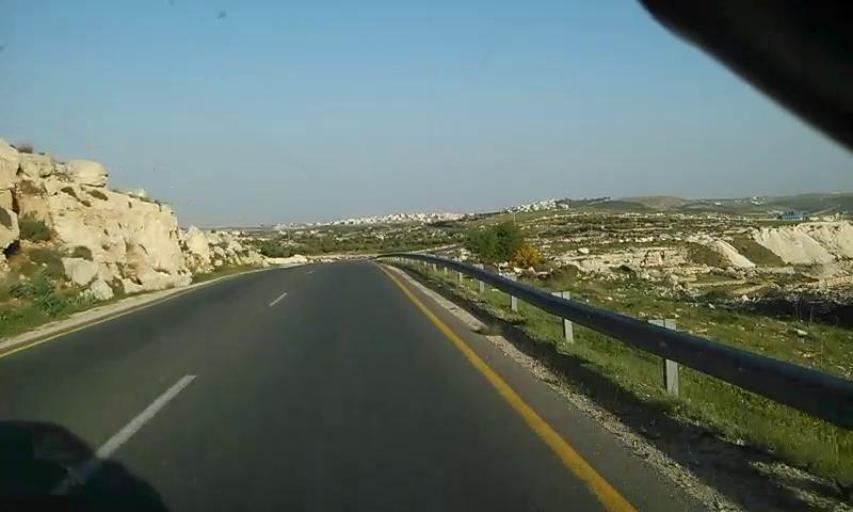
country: PS
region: West Bank
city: Marah Rabbah
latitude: 31.6477
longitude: 35.1844
